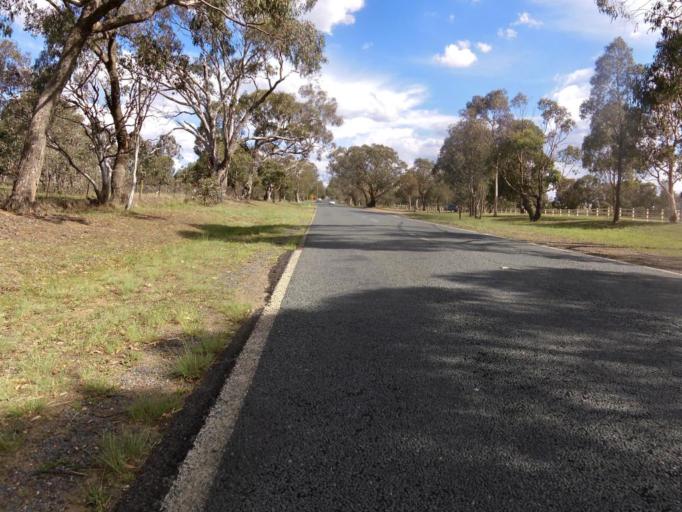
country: AU
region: Australian Capital Territory
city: Belconnen
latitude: -35.1783
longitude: 149.0727
